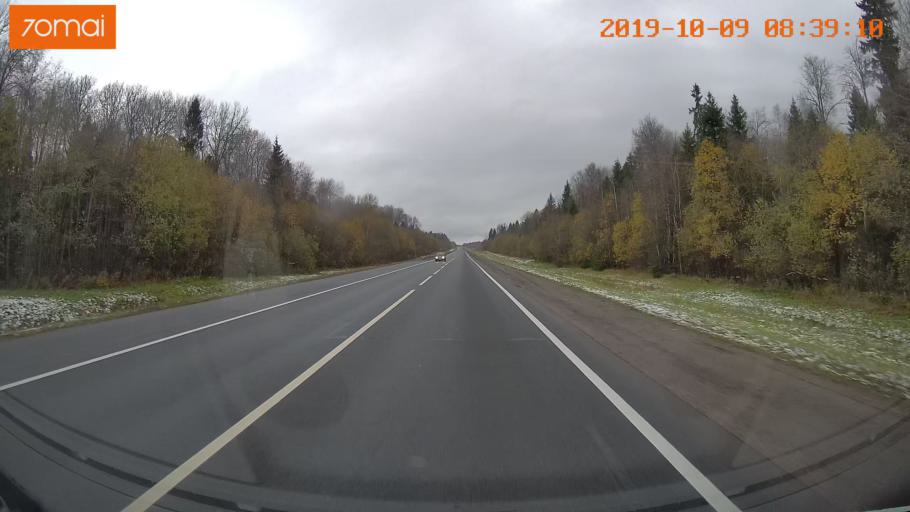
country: RU
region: Vologda
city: Gryazovets
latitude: 58.9674
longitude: 40.1566
